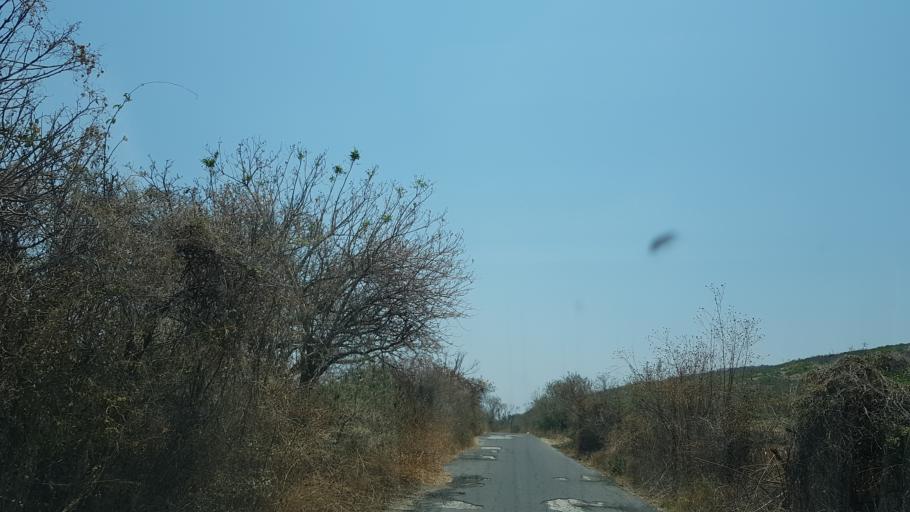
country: MX
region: Puebla
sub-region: Atzitzihuacan
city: San Miguel Aguacomulican
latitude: 18.7978
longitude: -98.5465
